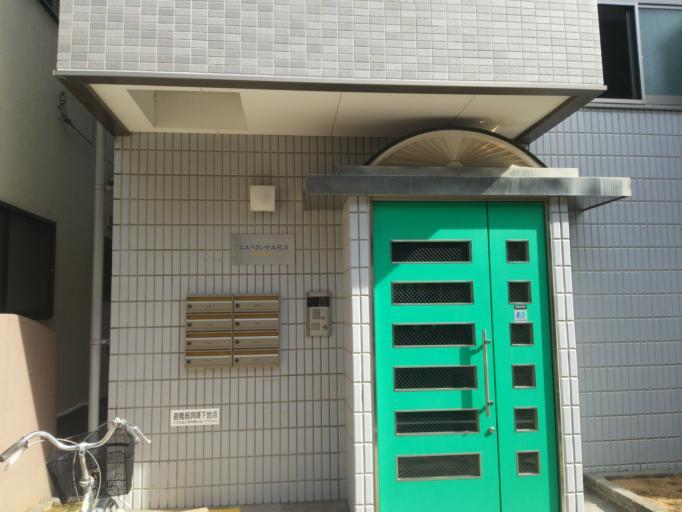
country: JP
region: Hyogo
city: Amagasaki
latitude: 34.7426
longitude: 135.4058
